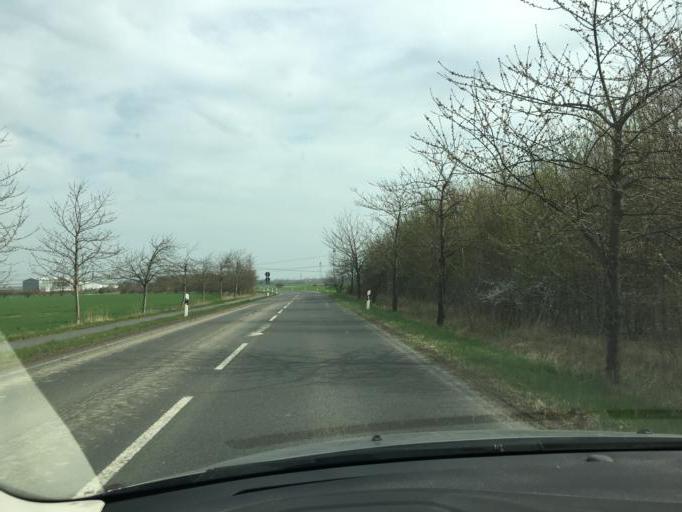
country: DE
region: Saxony
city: Taucha
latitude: 51.3598
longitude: 12.4913
